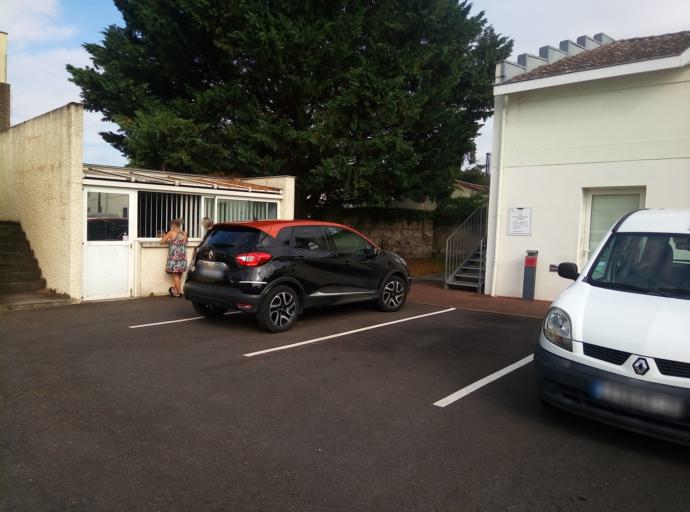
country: FR
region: Aquitaine
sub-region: Departement de la Gironde
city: Villenave-d'Ornon
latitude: 44.7831
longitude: -0.5717
